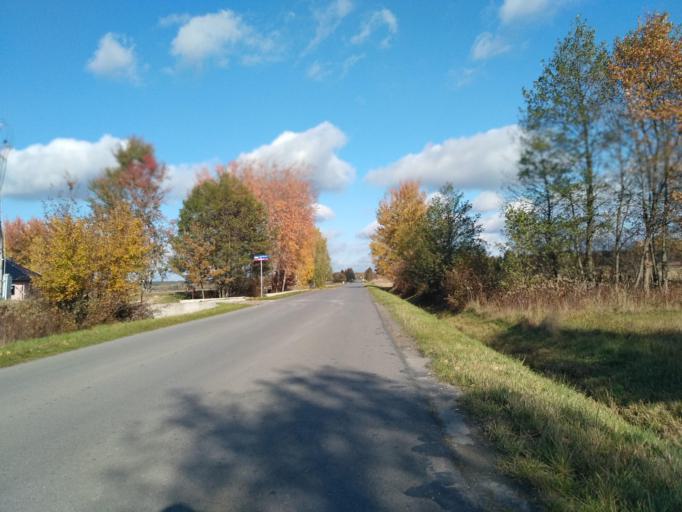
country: PL
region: Subcarpathian Voivodeship
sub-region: Powiat rzeszowski
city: Swilcza
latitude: 50.1223
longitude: 21.9008
